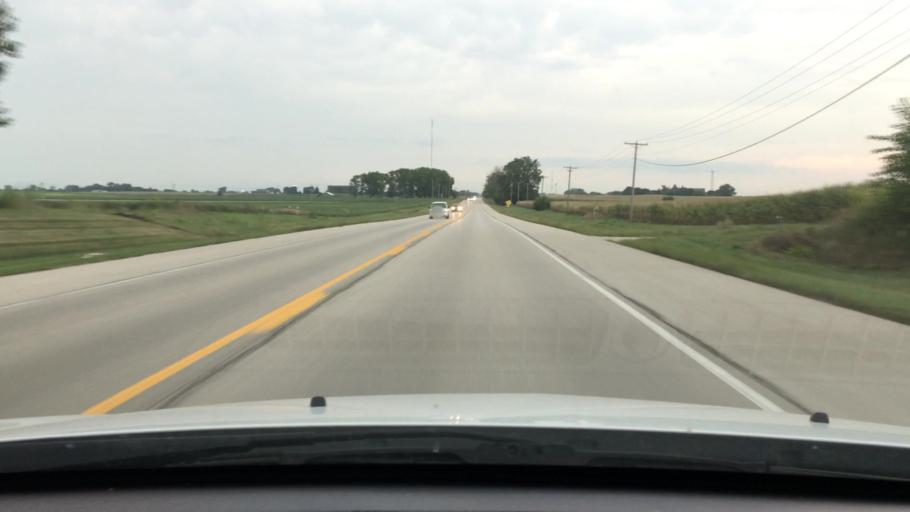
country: US
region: Illinois
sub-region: DeKalb County
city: DeKalb
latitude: 41.8600
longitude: -88.7538
